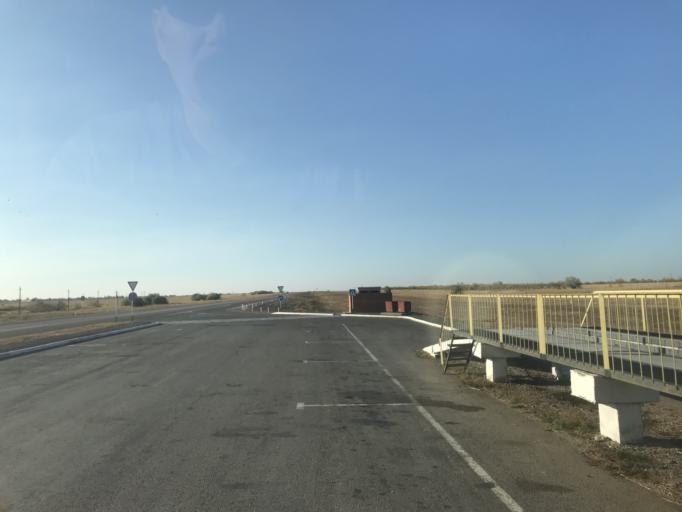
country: KZ
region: Pavlodar
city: Koktobe
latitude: 51.8828
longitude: 77.4188
